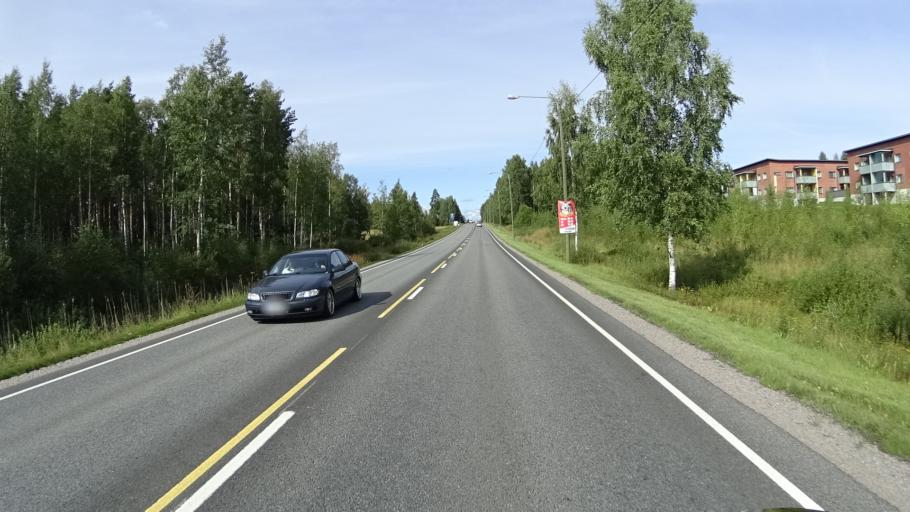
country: FI
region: Pirkanmaa
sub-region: Tampere
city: Haemeenkyroe
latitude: 61.6468
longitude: 23.1854
